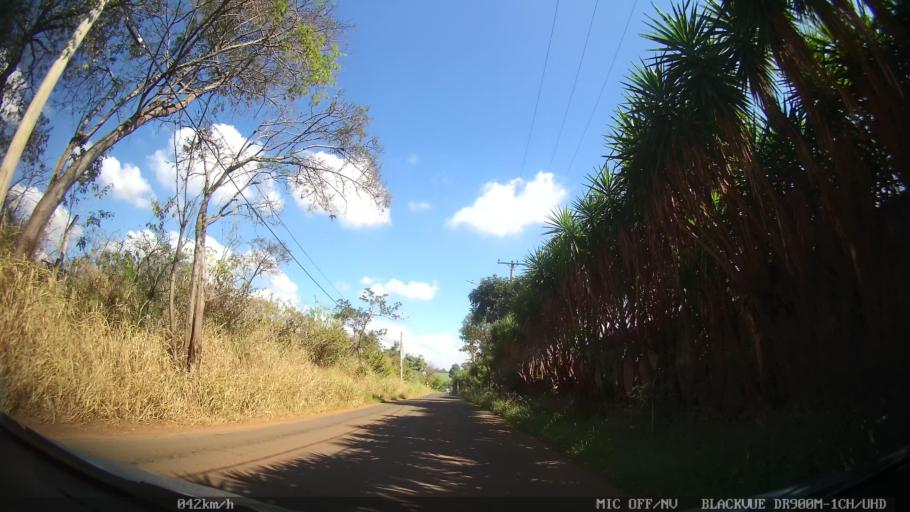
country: BR
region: Sao Paulo
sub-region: Hortolandia
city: Hortolandia
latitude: -22.8770
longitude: -47.2555
